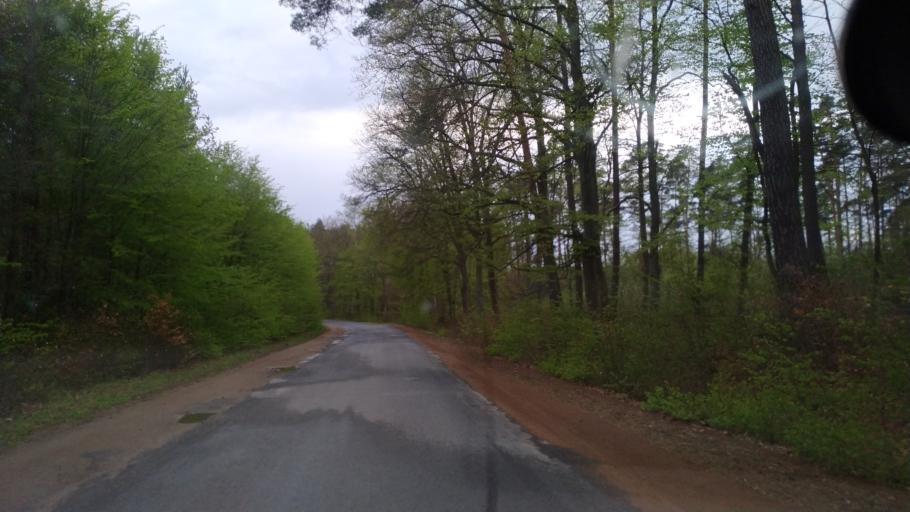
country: PL
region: Pomeranian Voivodeship
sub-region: Powiat starogardzki
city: Osiek
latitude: 53.7032
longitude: 18.5709
